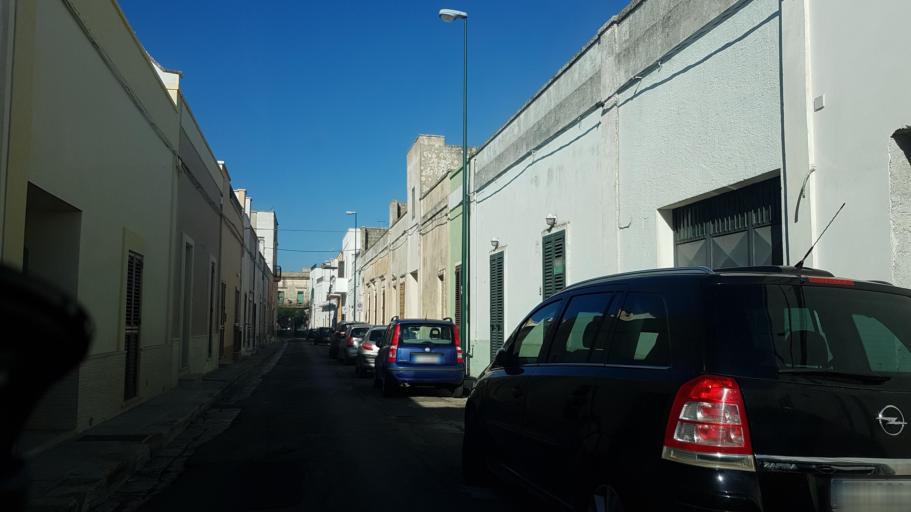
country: IT
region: Apulia
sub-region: Provincia di Lecce
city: Campi Salentina
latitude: 40.3971
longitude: 18.0194
